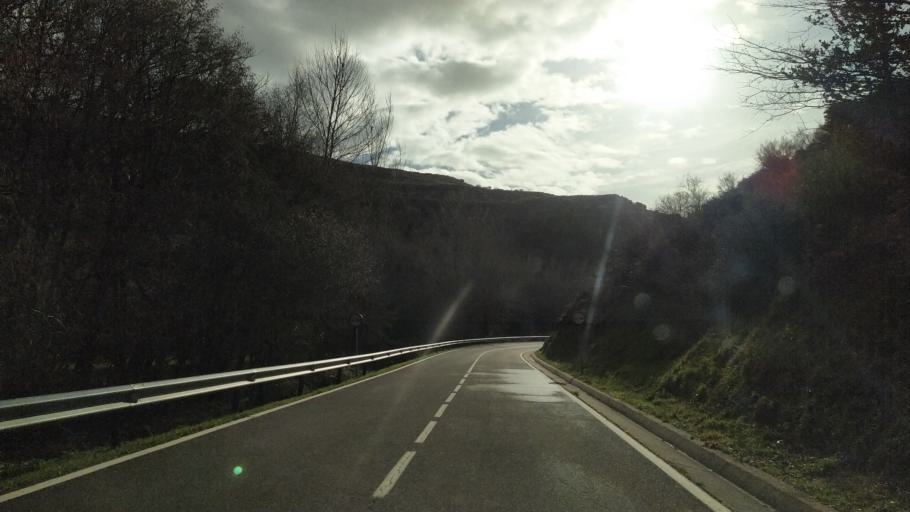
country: ES
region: Cantabria
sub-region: Provincia de Cantabria
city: San Martin de Elines
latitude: 42.8463
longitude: -3.9102
